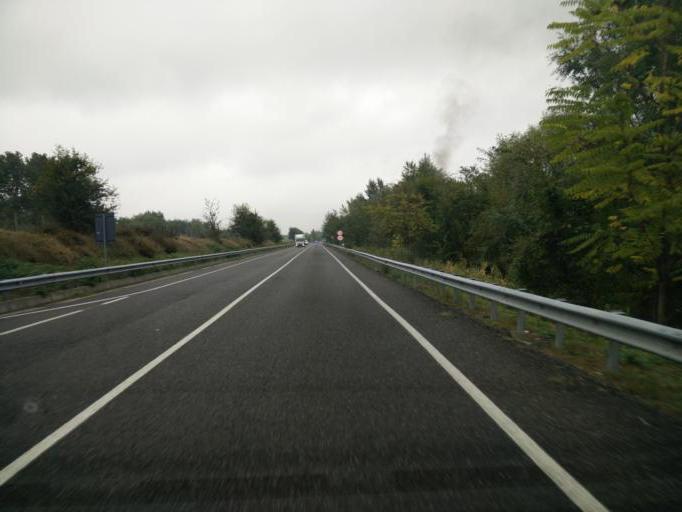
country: IT
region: Emilia-Romagna
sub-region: Provincia di Bologna
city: Borgonuovo
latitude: 44.4401
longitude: 11.2787
